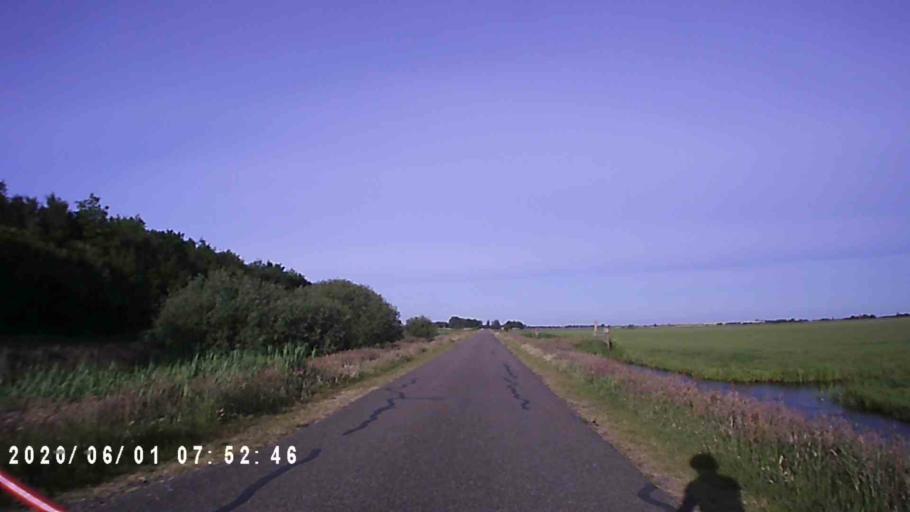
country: NL
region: Friesland
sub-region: Gemeente Dantumadiel
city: Rinsumageast
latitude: 53.2836
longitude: 5.9373
